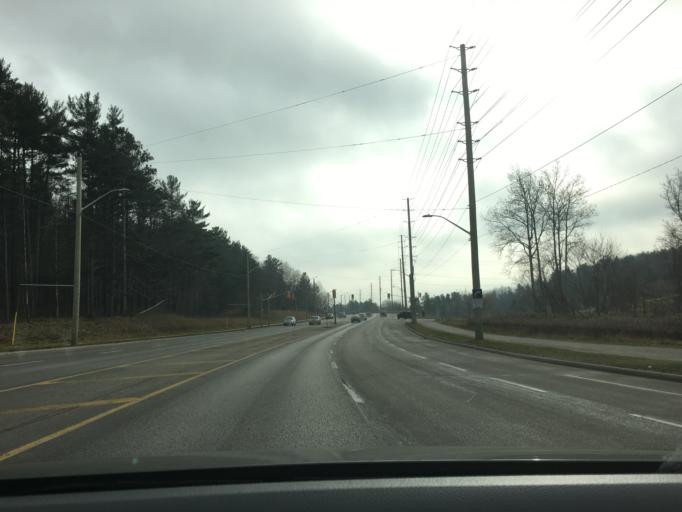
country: CA
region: Ontario
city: Barrie
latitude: 44.3873
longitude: -79.7300
